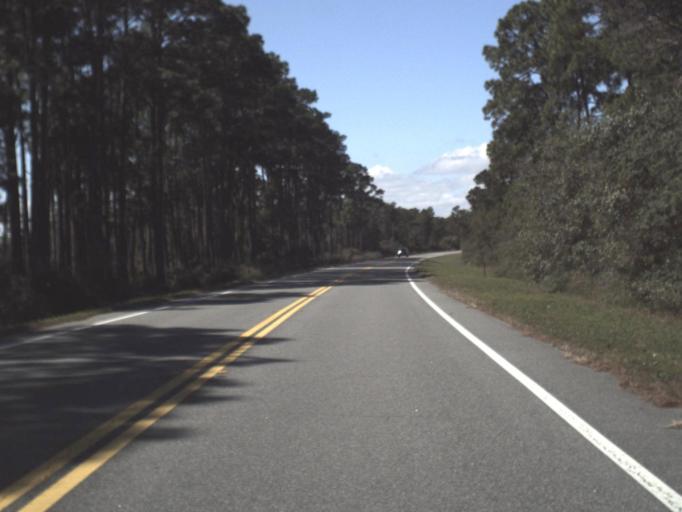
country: US
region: Florida
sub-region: Franklin County
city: Carrabelle
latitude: 29.9279
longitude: -84.4320
